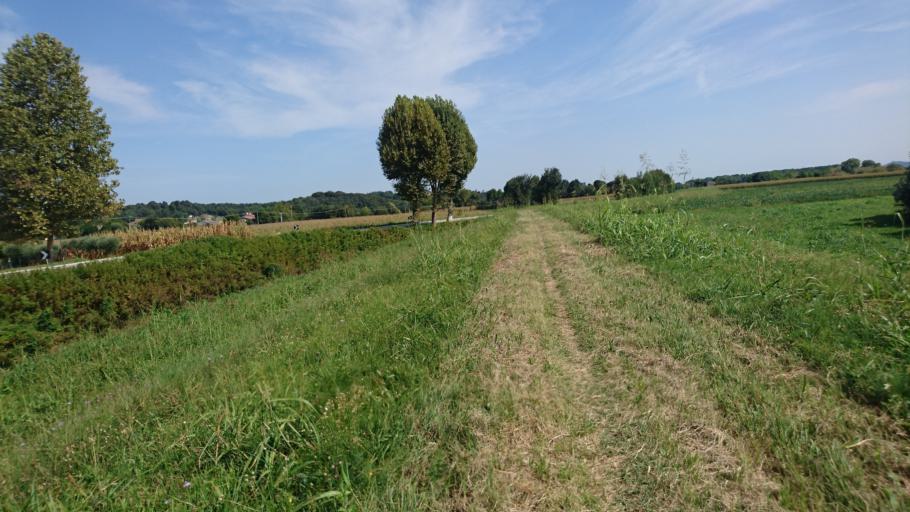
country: IT
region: Veneto
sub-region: Provincia di Vicenza
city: Montegalda
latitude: 45.4571
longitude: 11.6504
